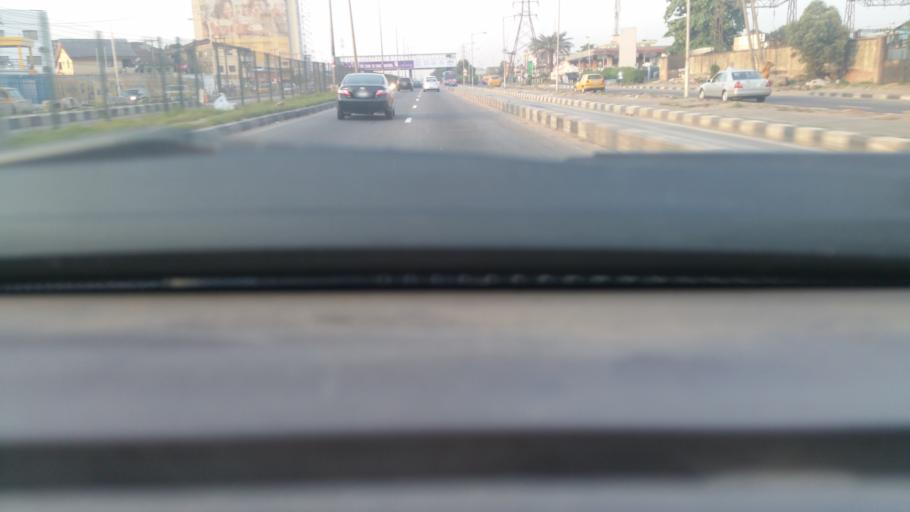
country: NG
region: Lagos
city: Somolu
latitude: 6.5307
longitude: 3.3674
